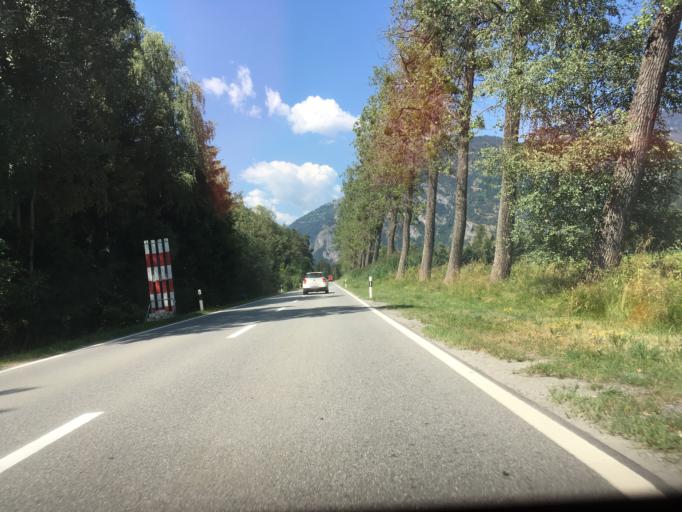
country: CH
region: Grisons
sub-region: Hinterrhein District
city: Cazis
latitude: 46.7418
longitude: 9.4264
